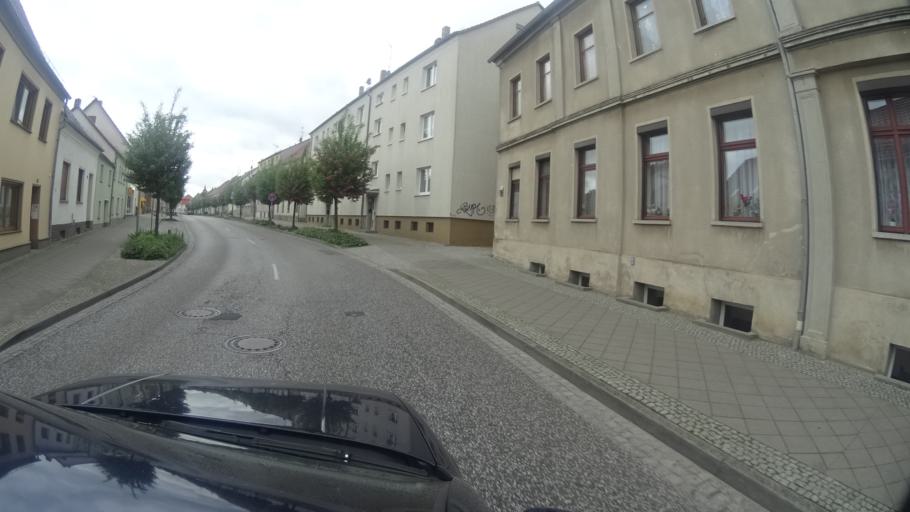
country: DE
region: Brandenburg
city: Fehrbellin
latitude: 52.8126
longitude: 12.7705
